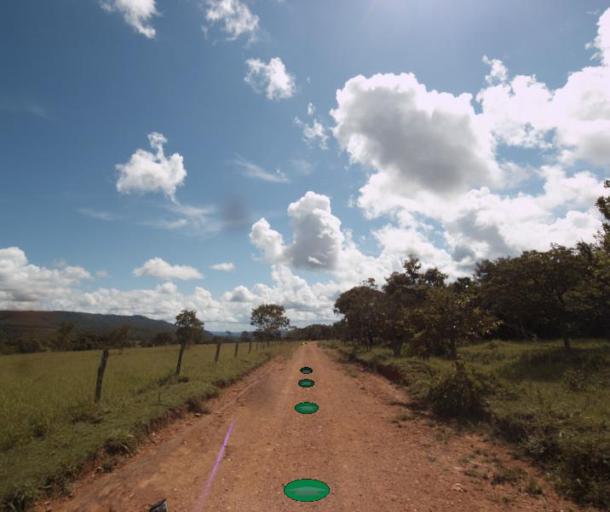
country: BR
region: Goias
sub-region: Pirenopolis
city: Pirenopolis
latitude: -15.7833
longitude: -48.9331
